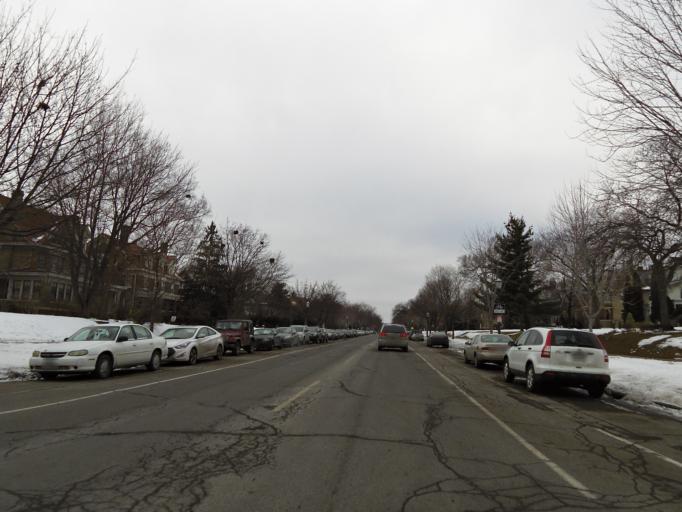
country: US
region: Minnesota
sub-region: Dakota County
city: West Saint Paul
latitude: 44.9414
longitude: -93.1390
